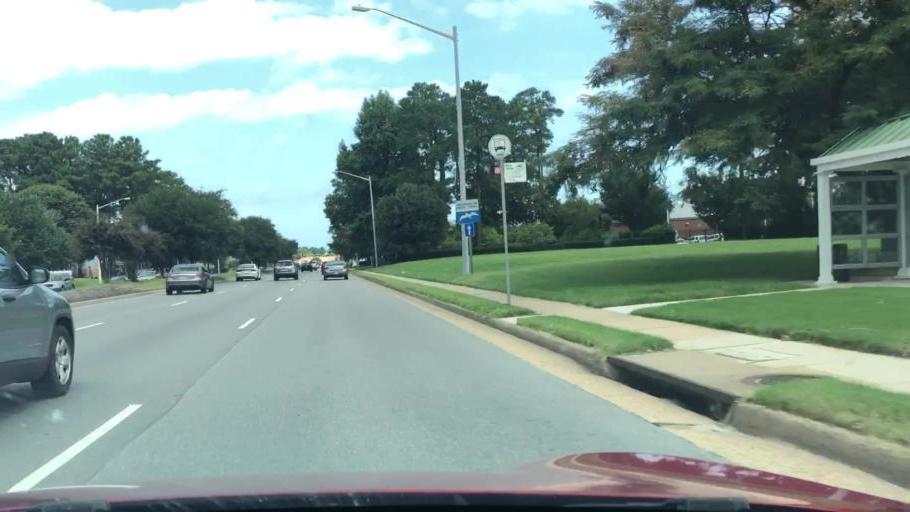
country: US
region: Virginia
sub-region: City of Chesapeake
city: Chesapeake
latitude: 36.8684
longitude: -76.1329
